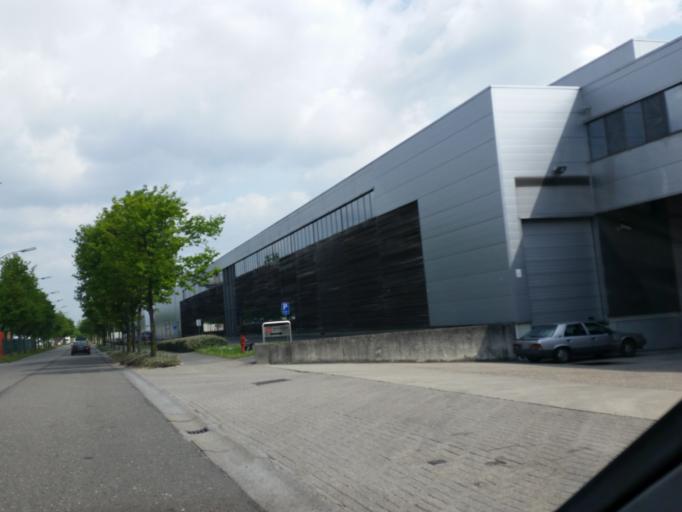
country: BE
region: Flanders
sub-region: Provincie Vlaams-Brabant
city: Zemst
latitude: 51.0041
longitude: 4.4643
